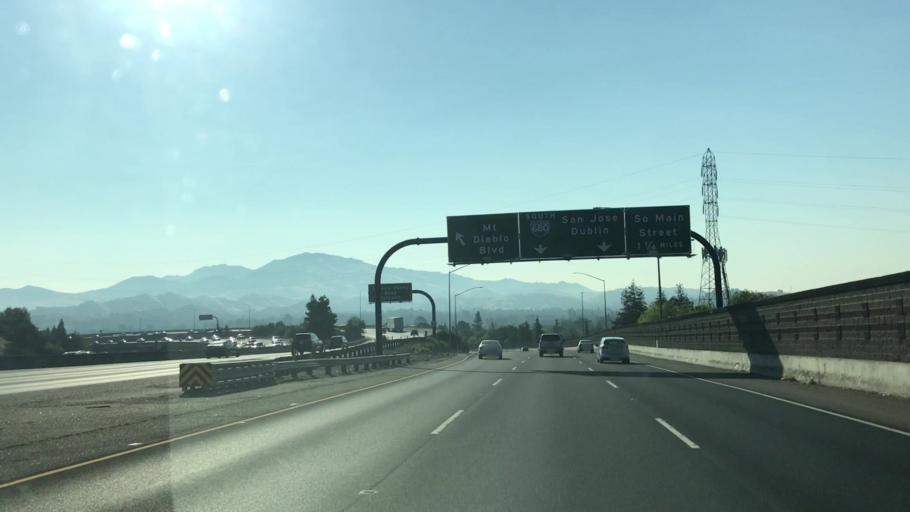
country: US
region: California
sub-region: Contra Costa County
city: Saranap
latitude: 37.8963
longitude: -122.0784
